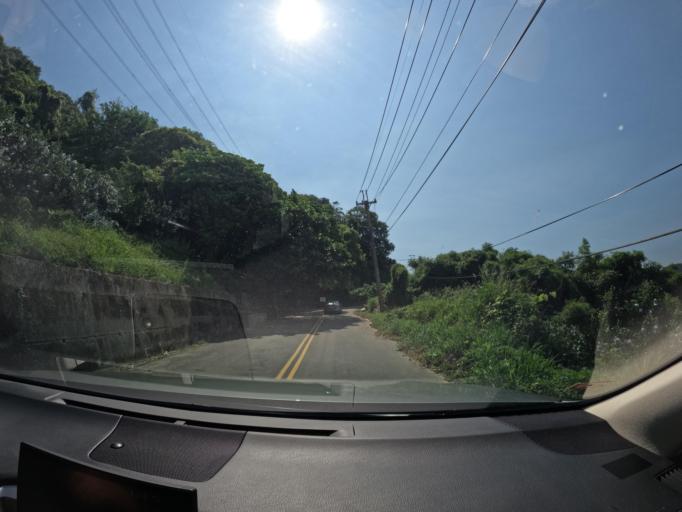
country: TW
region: Taiwan
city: Fengyuan
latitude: 24.3147
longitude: 120.7726
